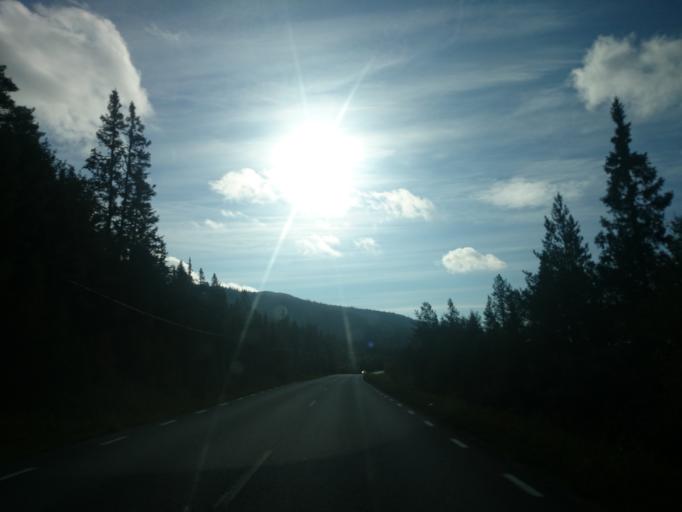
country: SE
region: Jaemtland
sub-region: Are Kommun
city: Are
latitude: 62.5962
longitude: 12.5366
